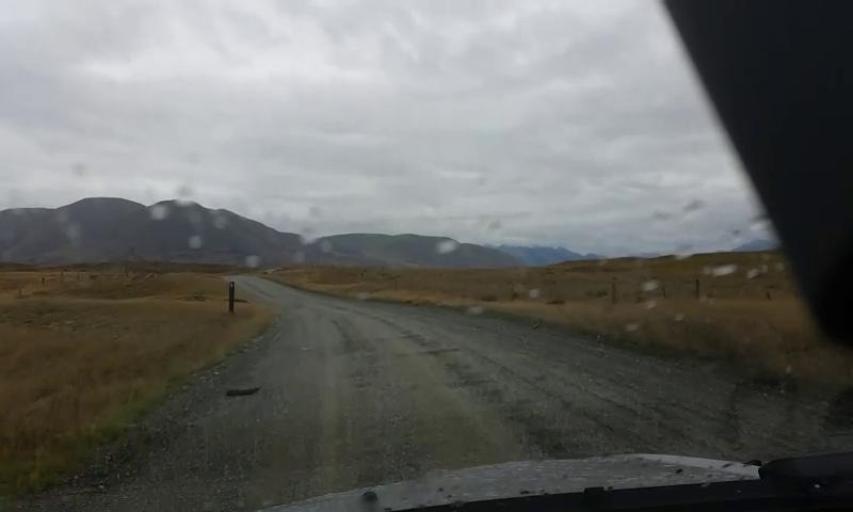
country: NZ
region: Canterbury
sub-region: Ashburton District
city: Methven
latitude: -43.6149
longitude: 171.1044
